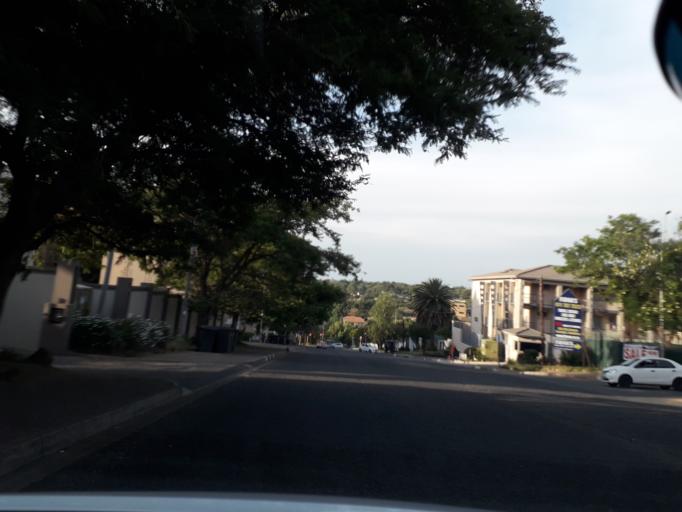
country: ZA
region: Gauteng
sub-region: City of Johannesburg Metropolitan Municipality
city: Johannesburg
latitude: -26.0911
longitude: 28.0007
